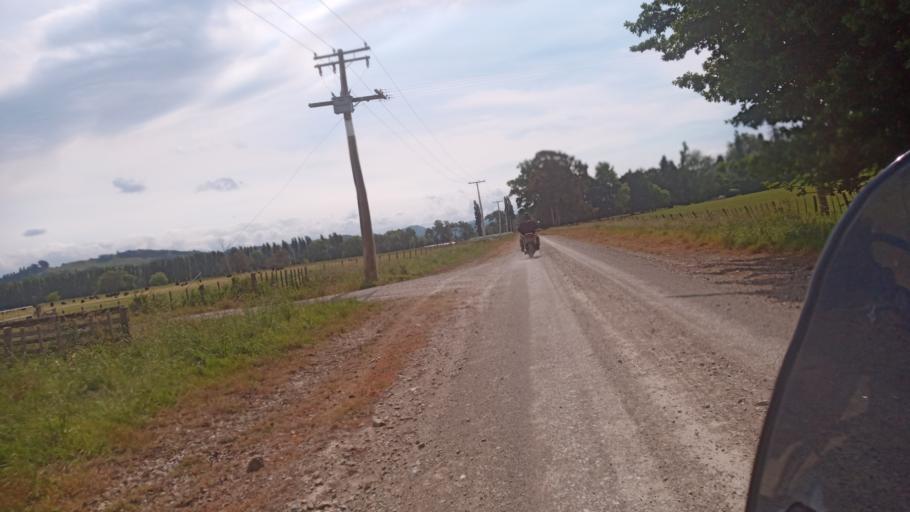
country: NZ
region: Gisborne
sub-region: Gisborne District
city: Gisborne
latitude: -38.4685
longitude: 177.8526
